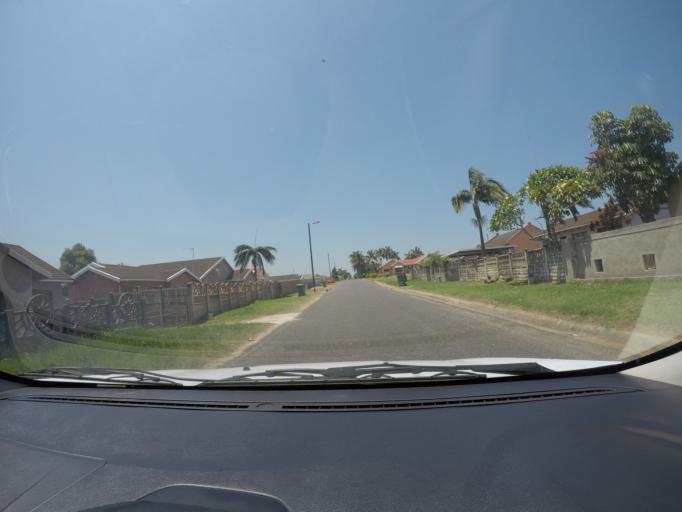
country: ZA
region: KwaZulu-Natal
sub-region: uThungulu District Municipality
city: eSikhawini
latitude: -28.8891
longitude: 31.8825
